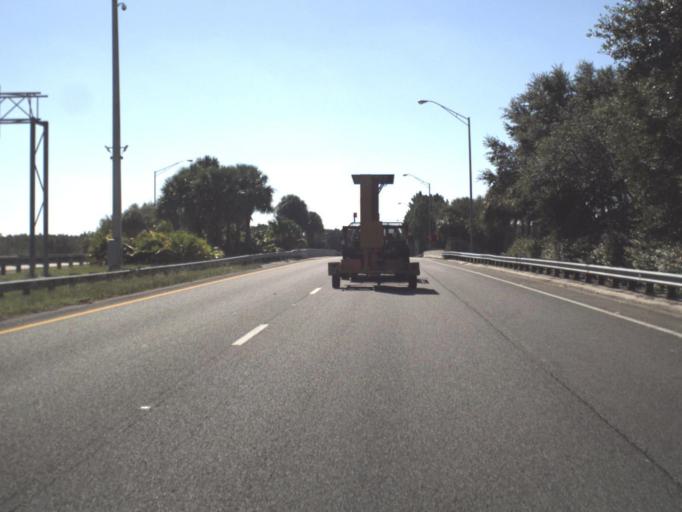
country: US
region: Florida
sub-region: Hillsborough County
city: Greater Northdale
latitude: 28.0931
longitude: -82.5449
